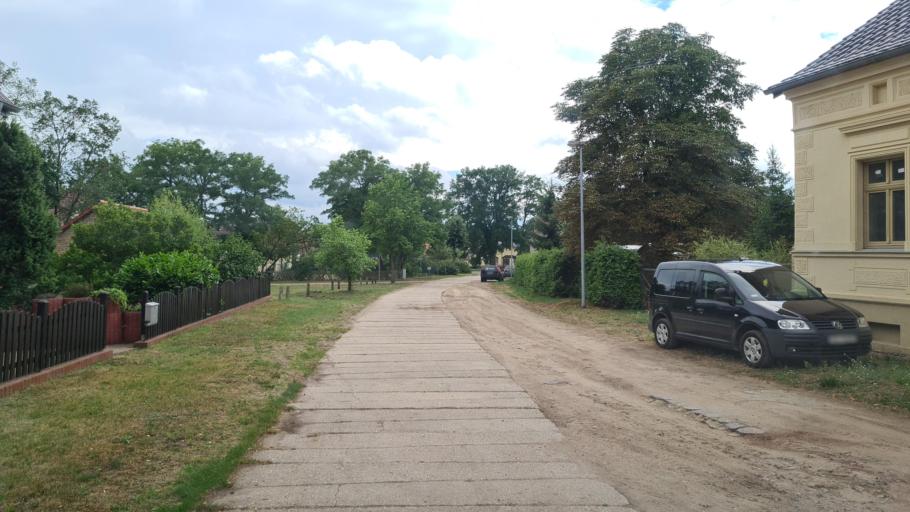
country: DE
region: Brandenburg
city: Trebbin
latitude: 52.2414
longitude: 13.1678
